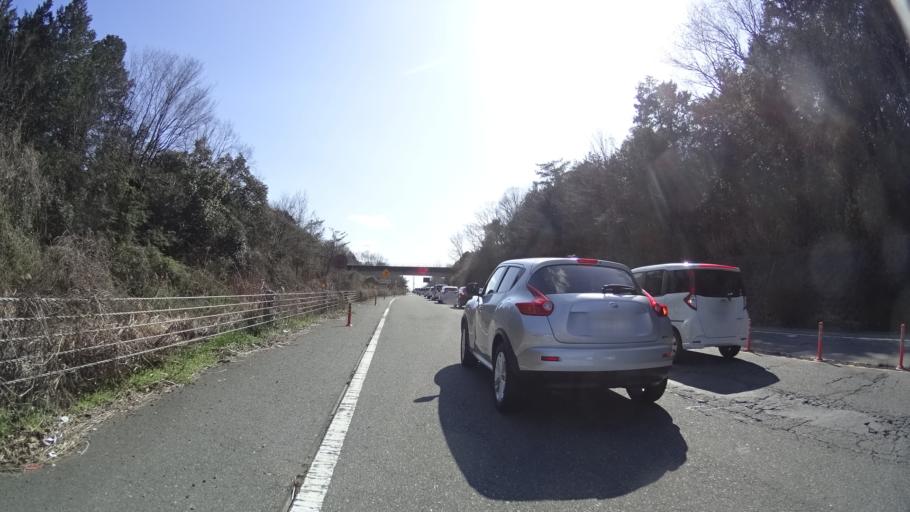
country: JP
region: Shiga Prefecture
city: Kitahama
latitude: 35.1296
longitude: 135.9019
